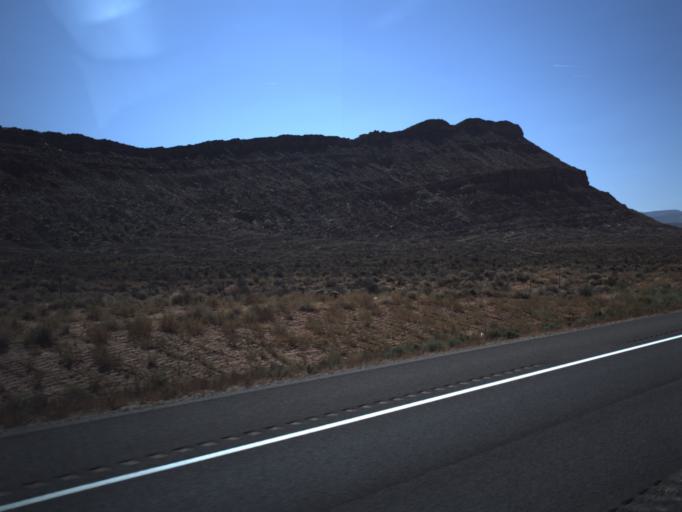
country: US
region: Utah
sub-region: Washington County
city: Washington
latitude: 37.0917
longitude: -113.4714
